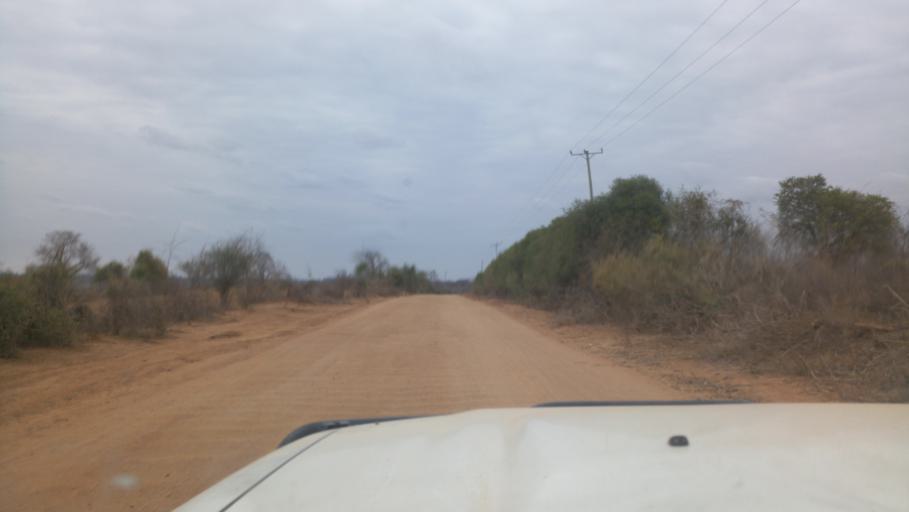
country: KE
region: Makueni
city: Makueni
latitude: -1.9793
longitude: 38.1032
